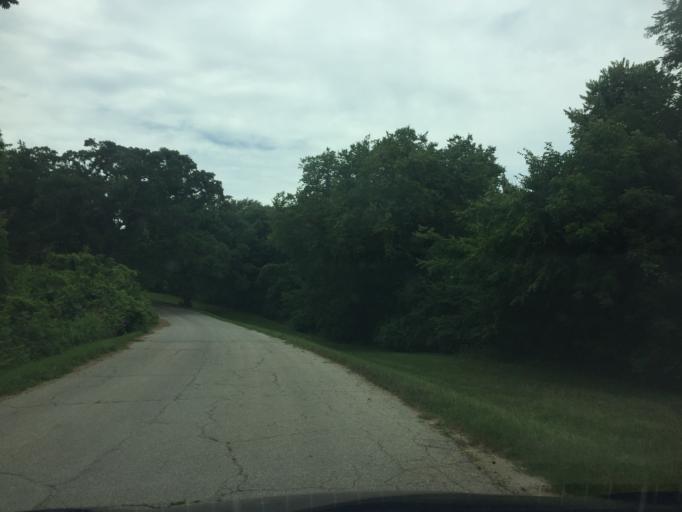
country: US
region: Missouri
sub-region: Platte County
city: Weston
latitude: 39.3714
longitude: -94.9259
